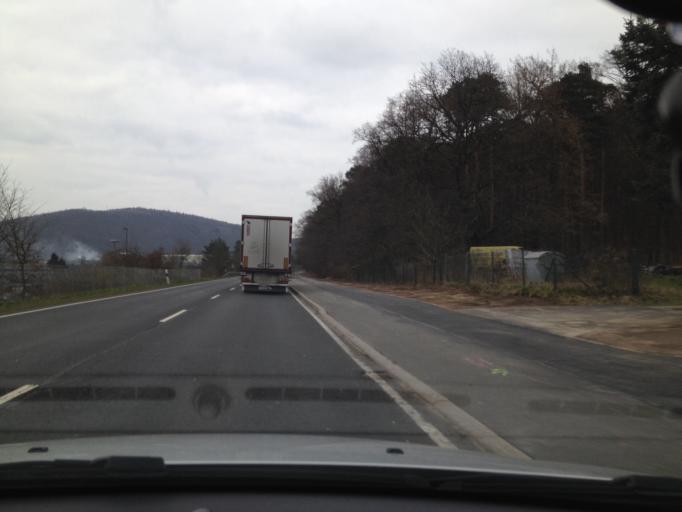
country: DE
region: Bavaria
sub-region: Regierungsbezirk Unterfranken
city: Hasloch
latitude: 49.7812
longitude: 9.4829
